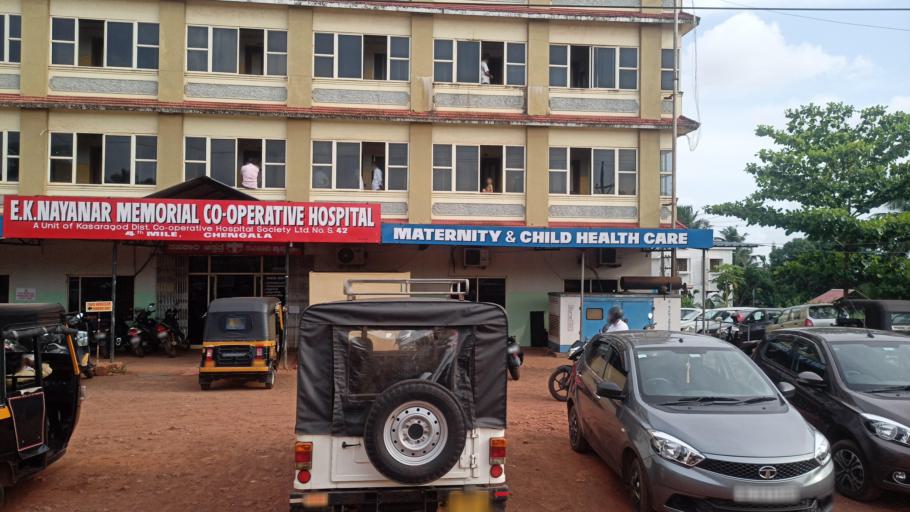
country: IN
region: Kerala
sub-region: Kasaragod District
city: Kasaragod
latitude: 12.5104
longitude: 75.0352
